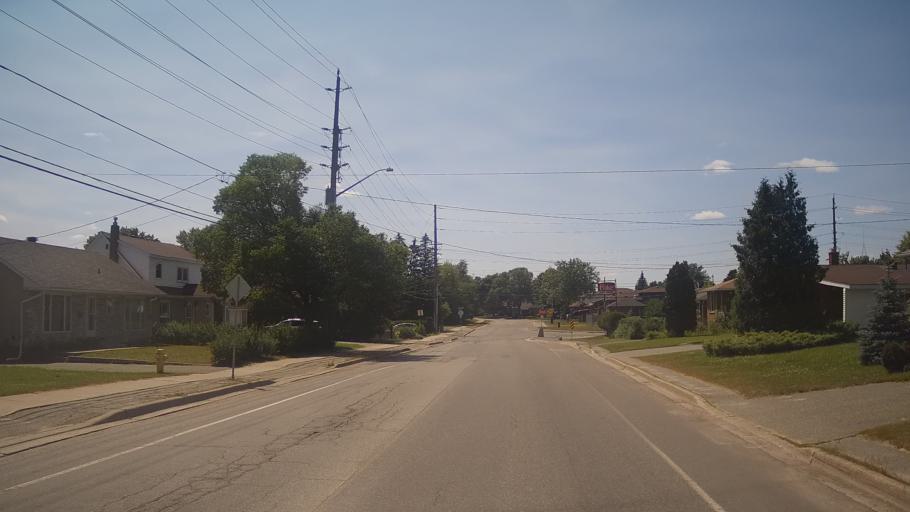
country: CA
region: Ontario
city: Greater Sudbury
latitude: 46.4600
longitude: -81.0266
